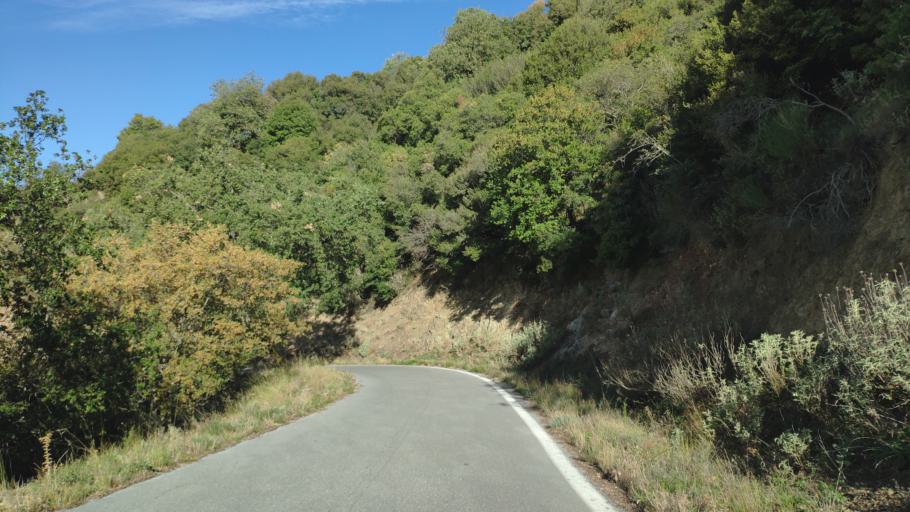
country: GR
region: Peloponnese
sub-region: Nomos Arkadias
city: Dimitsana
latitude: 37.5509
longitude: 22.0591
